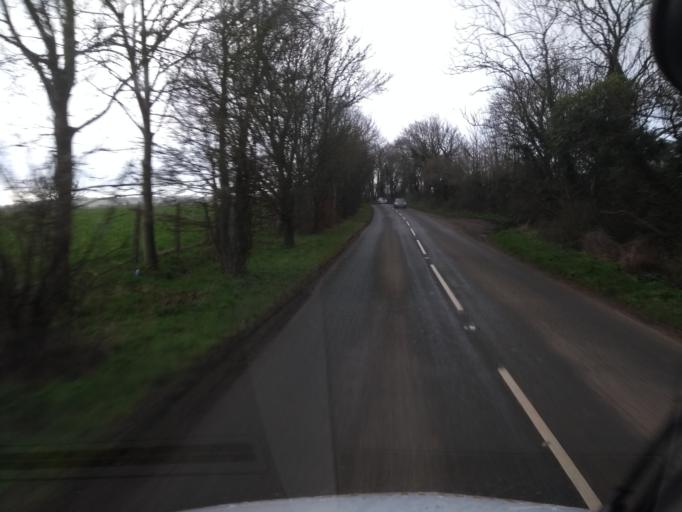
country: GB
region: England
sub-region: Somerset
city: Bruton
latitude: 51.0947
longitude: -2.4653
